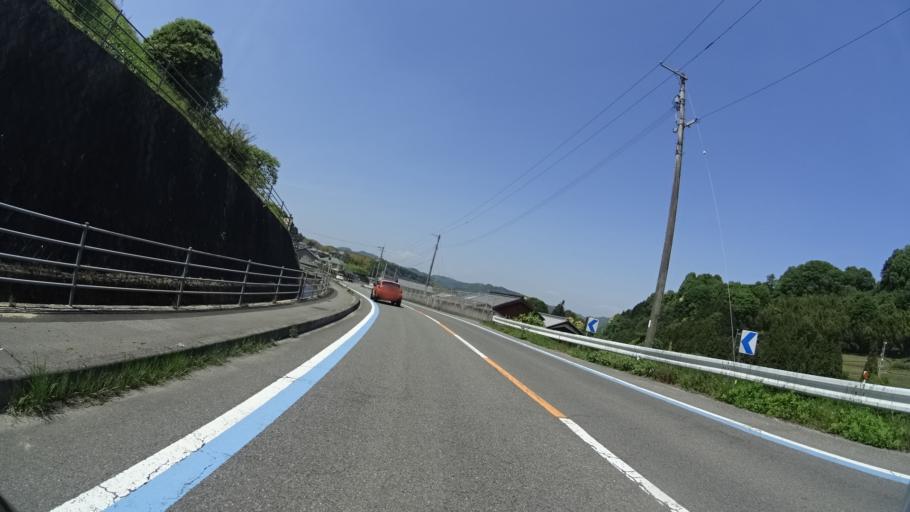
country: JP
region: Ehime
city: Hojo
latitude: 34.0048
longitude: 132.9387
